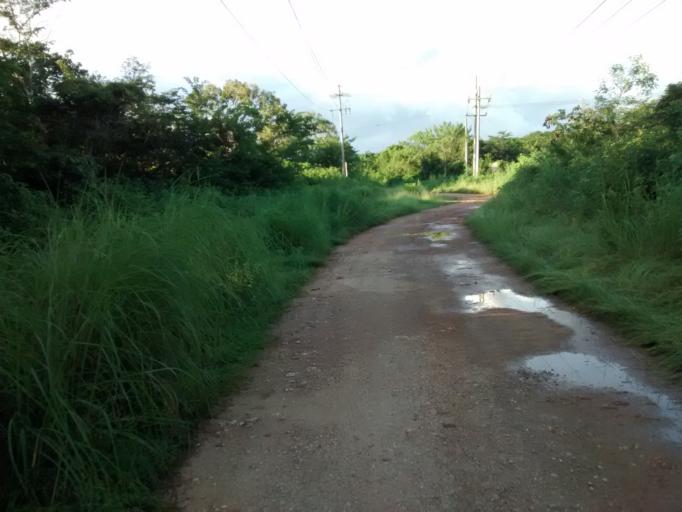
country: MX
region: Yucatan
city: Valladolid
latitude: 20.7060
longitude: -88.2061
